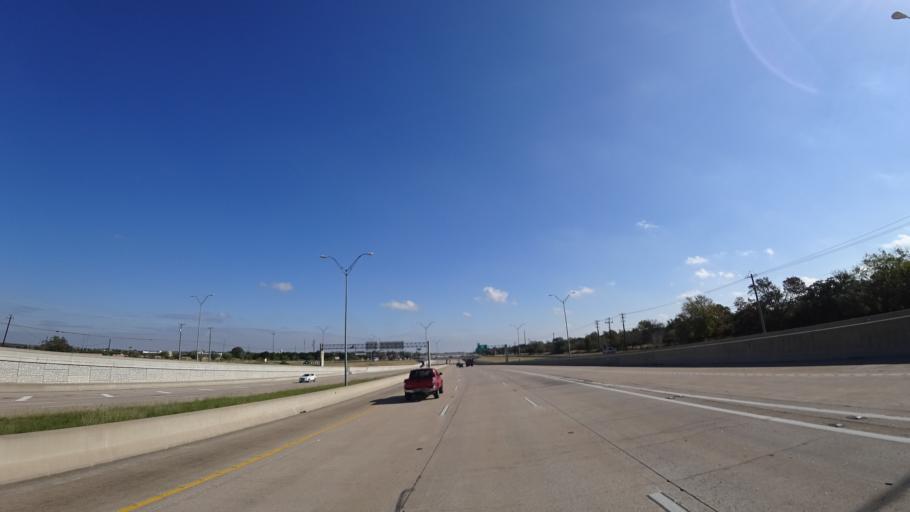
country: US
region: Texas
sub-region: Williamson County
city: Jollyville
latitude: 30.4748
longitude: -97.7693
